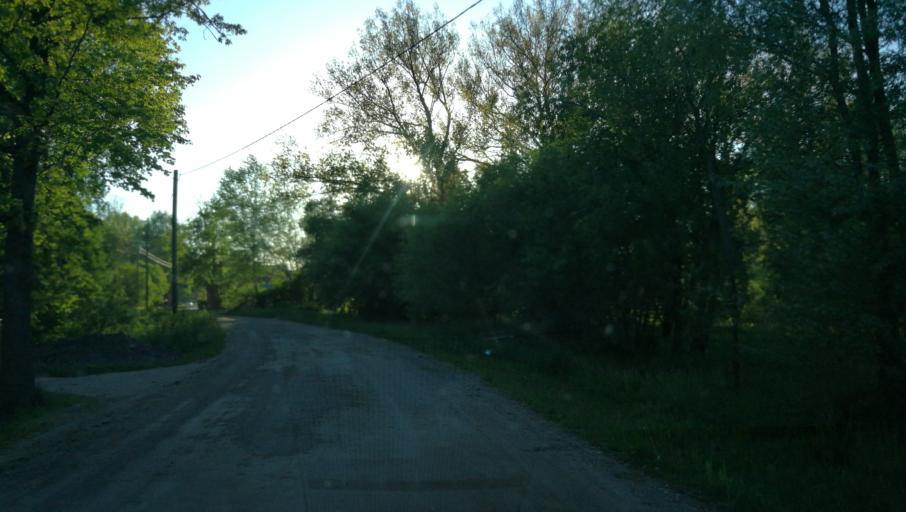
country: LV
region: Dobeles Rajons
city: Dobele
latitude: 56.6205
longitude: 23.2935
